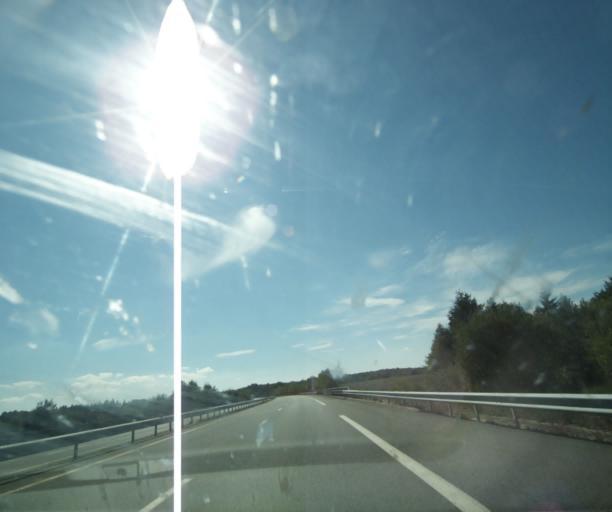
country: FR
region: Limousin
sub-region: Departement de la Correze
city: Correze
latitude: 45.3350
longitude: 1.8962
